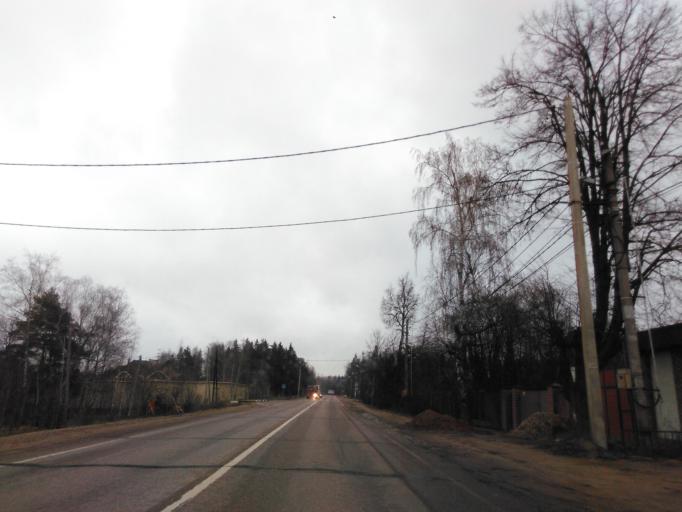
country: RU
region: Moskovskaya
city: Rozhdestveno
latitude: 55.8372
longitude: 37.0129
